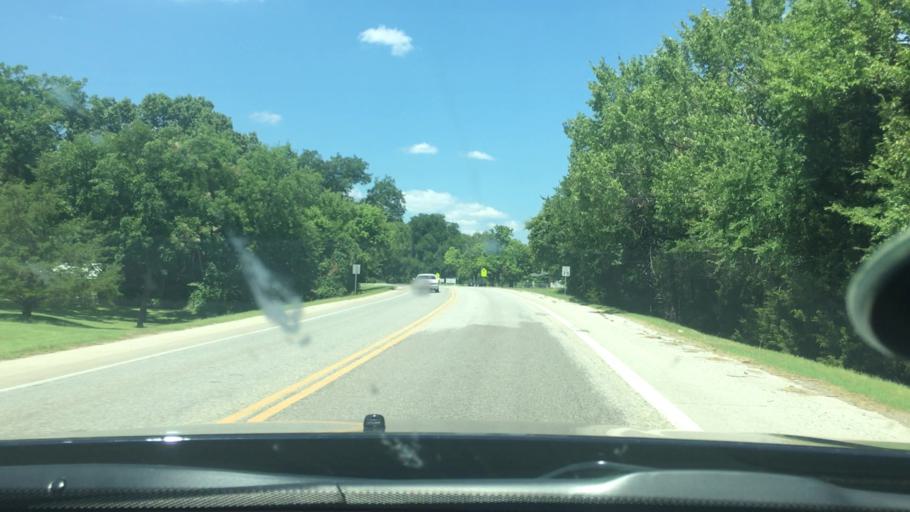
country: US
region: Oklahoma
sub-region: Carter County
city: Dickson
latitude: 34.1857
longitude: -96.8739
